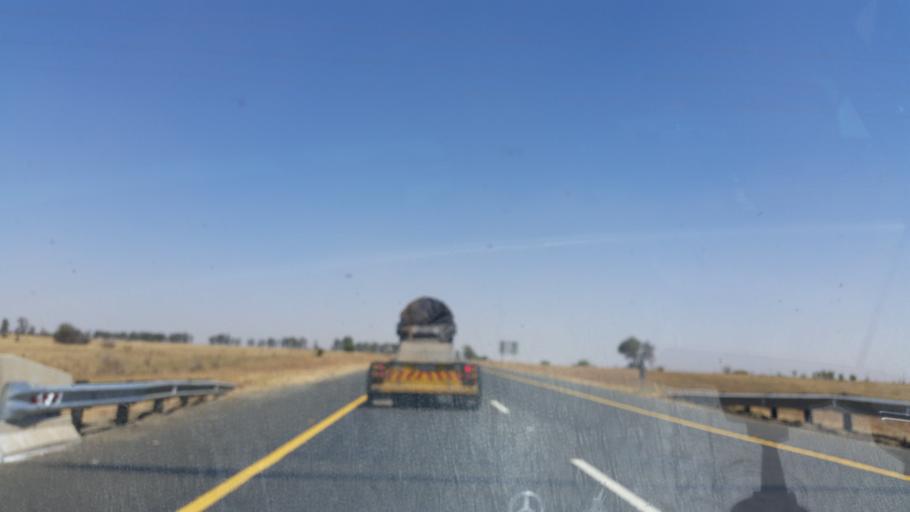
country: ZA
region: Orange Free State
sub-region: Lejweleputswa District Municipality
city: Winburg
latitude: -28.6356
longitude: 26.8977
